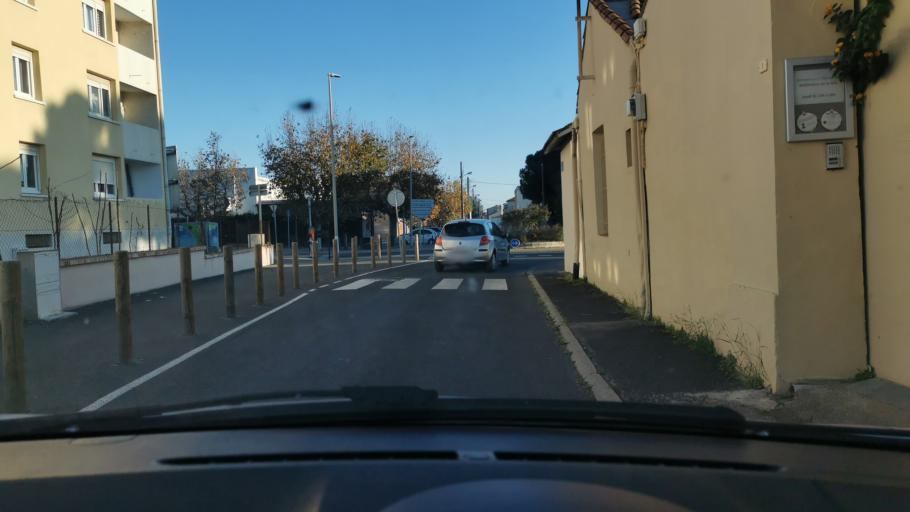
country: FR
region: Languedoc-Roussillon
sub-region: Departement de l'Herault
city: Frontignan
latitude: 43.4492
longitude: 3.7509
